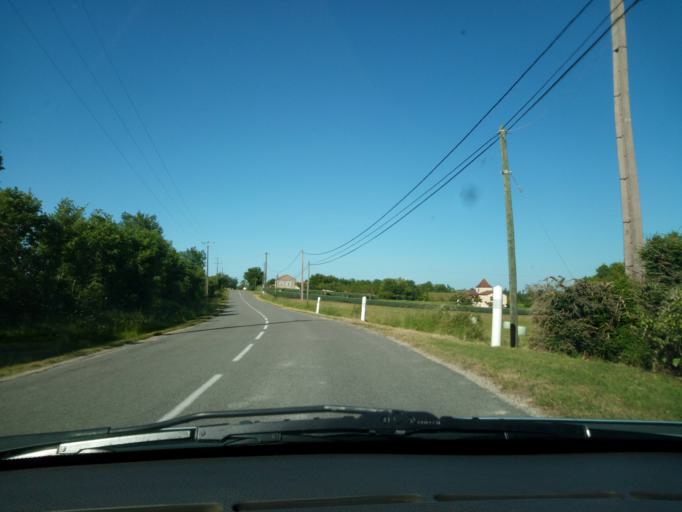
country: FR
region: Midi-Pyrenees
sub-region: Departement du Lot
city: Lalbenque
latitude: 44.3253
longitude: 1.4569
